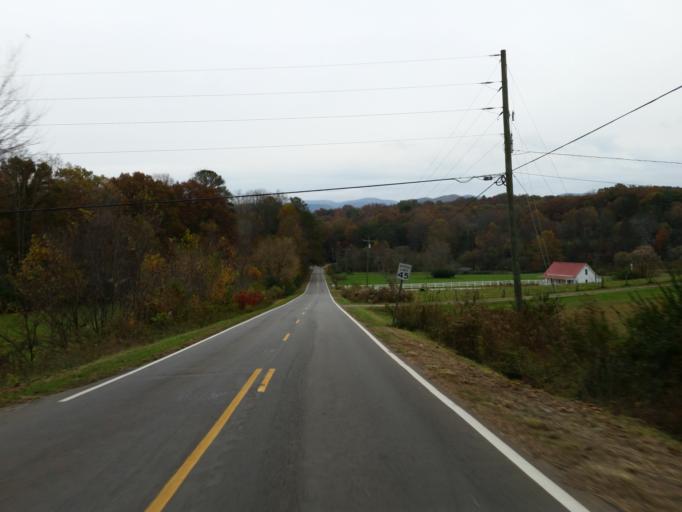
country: US
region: Georgia
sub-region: Gilmer County
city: Ellijay
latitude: 34.6446
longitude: -84.3400
